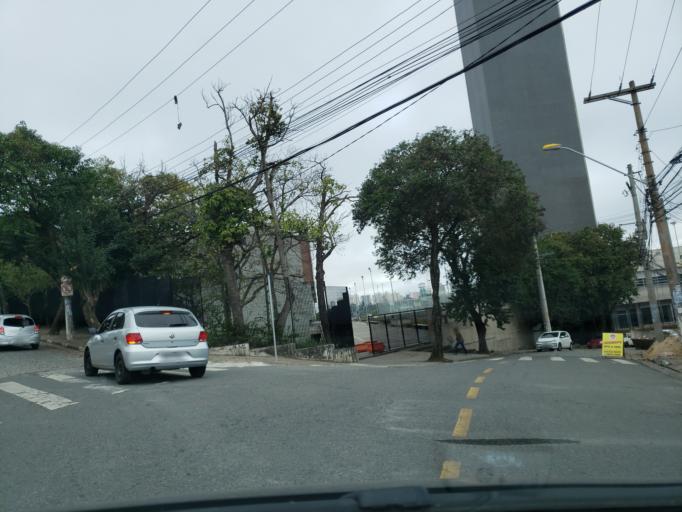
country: BR
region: Sao Paulo
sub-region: Santo Andre
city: Santo Andre
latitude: -23.6430
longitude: -46.5293
